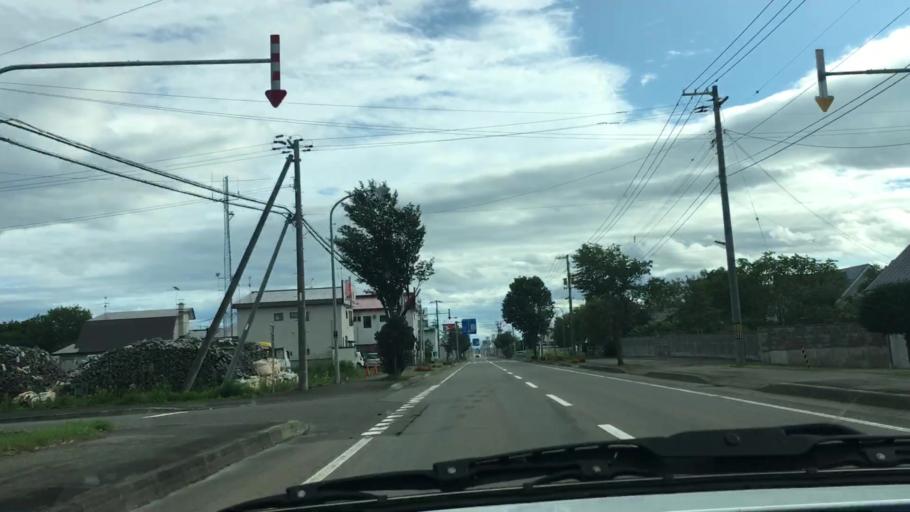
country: JP
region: Hokkaido
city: Otofuke
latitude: 43.2383
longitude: 143.2963
